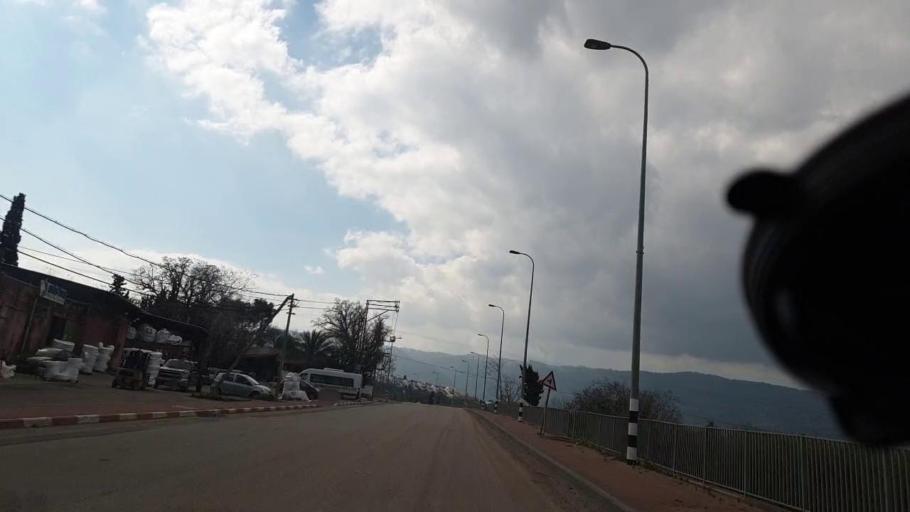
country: IL
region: Haifa
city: Ibtin
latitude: 32.7652
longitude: 35.1071
